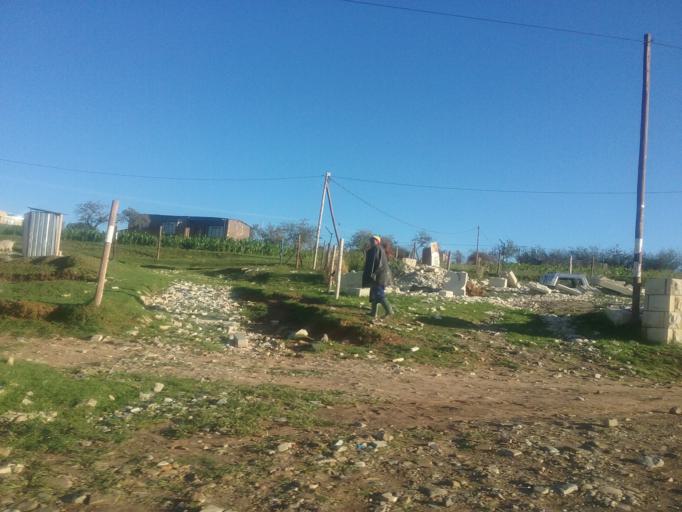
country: LS
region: Berea
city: Teyateyaneng
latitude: -29.1477
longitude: 27.6872
